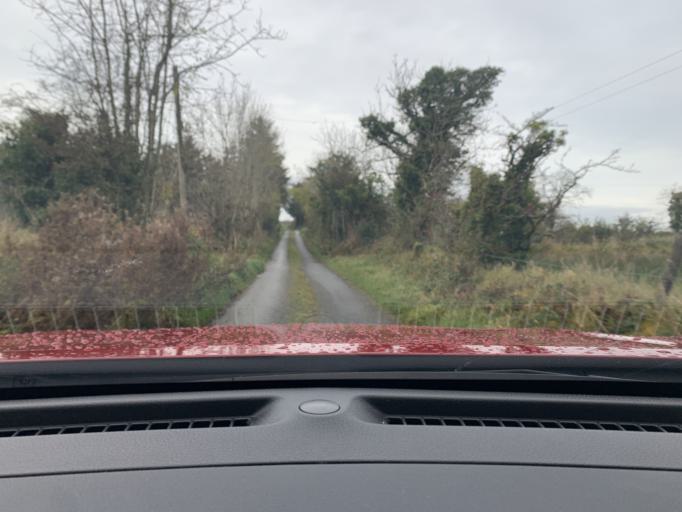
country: IE
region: Connaught
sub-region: Roscommon
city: Ballaghaderreen
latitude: 53.9168
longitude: -8.5669
